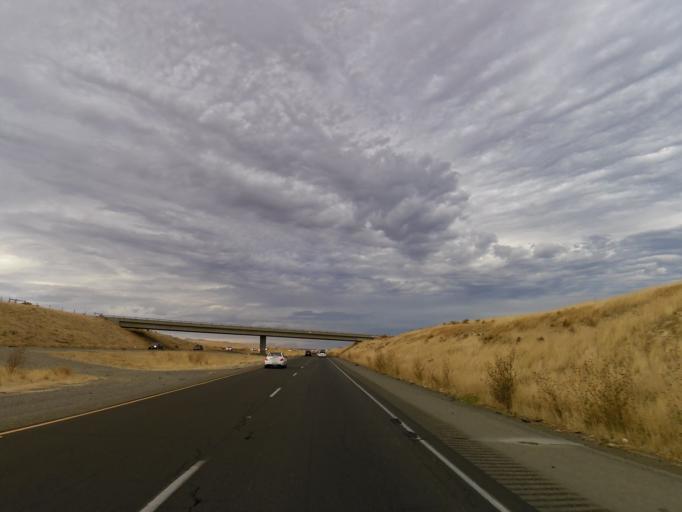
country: US
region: California
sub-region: Fresno County
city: Coalinga
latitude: 36.3296
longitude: -120.2990
